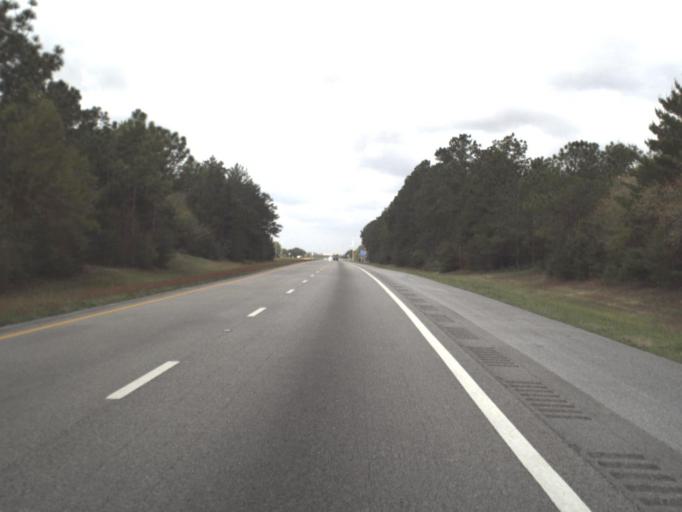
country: US
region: Florida
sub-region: Okaloosa County
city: Crestview
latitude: 30.7269
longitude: -86.4956
